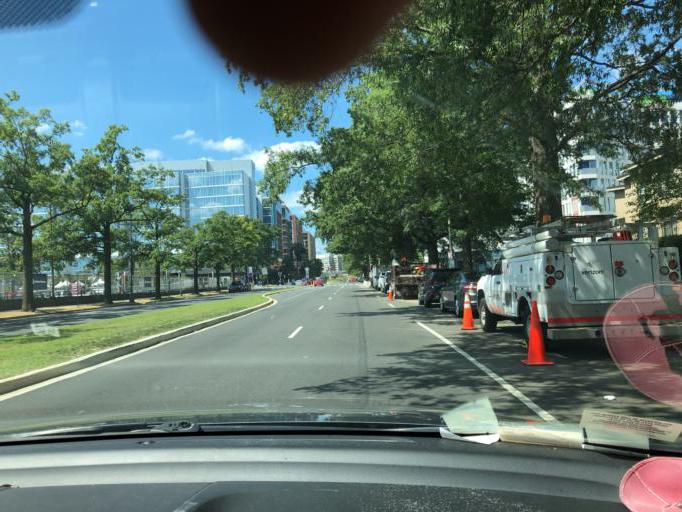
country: US
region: Washington, D.C.
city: Washington, D.C.
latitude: 38.8777
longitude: -77.0214
